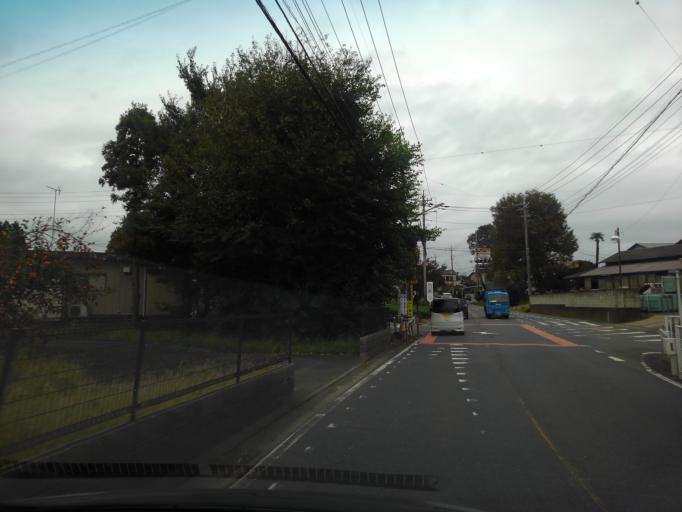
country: JP
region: Saitama
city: Tokorozawa
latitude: 35.7896
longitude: 139.4153
